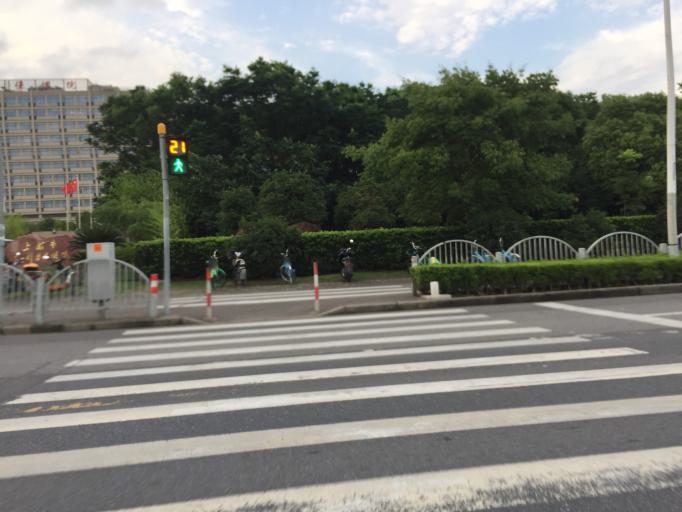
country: CN
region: Shanghai Shi
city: Huamu
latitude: 31.1904
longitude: 121.5463
